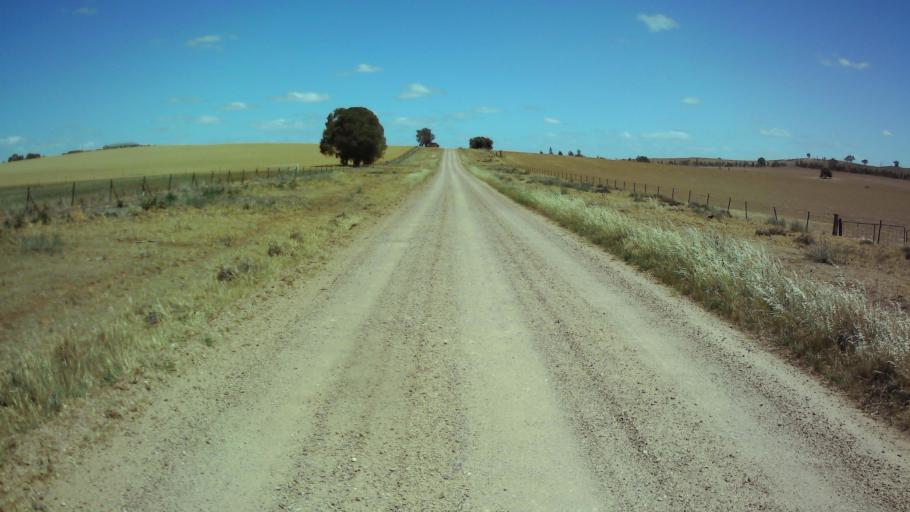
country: AU
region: New South Wales
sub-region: Weddin
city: Grenfell
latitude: -33.9459
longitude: 148.3293
